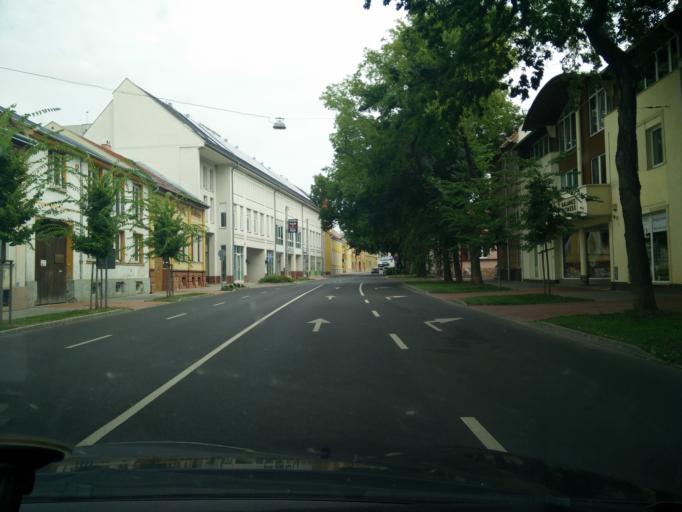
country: HU
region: Hajdu-Bihar
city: Debrecen
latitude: 47.5254
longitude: 21.6235
